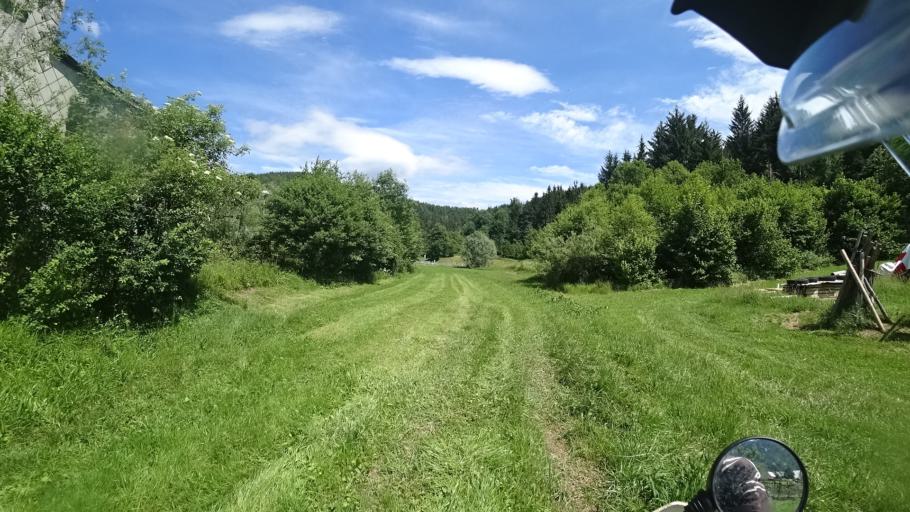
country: SI
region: Osilnica
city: Osilnica
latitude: 45.5140
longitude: 14.6458
